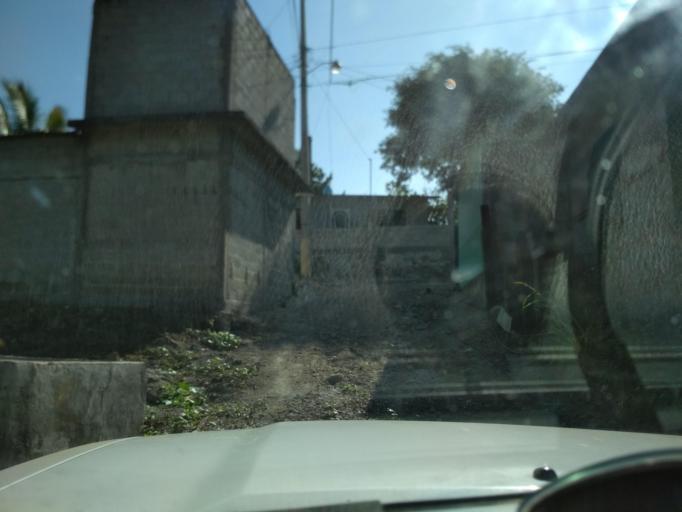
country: MX
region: Veracruz
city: Rinconada
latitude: 19.3562
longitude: -96.5608
